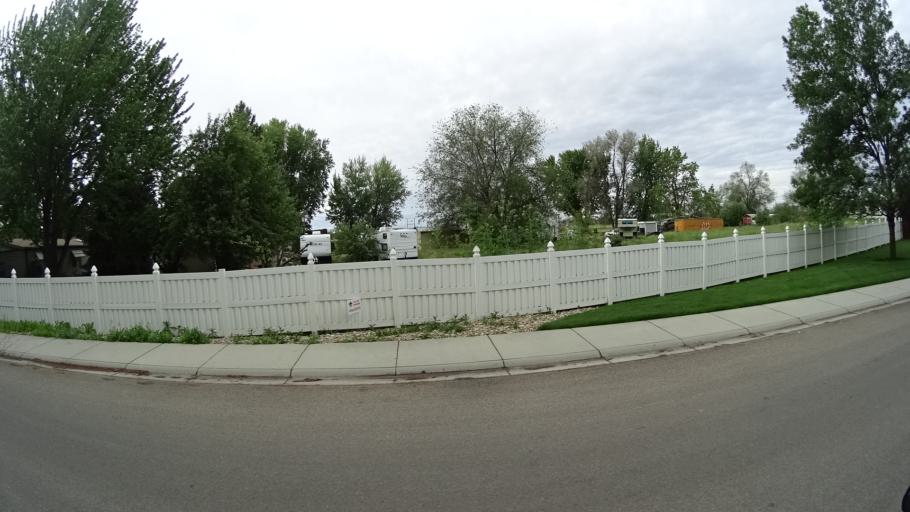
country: US
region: Idaho
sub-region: Ada County
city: Star
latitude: 43.6958
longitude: -116.4988
